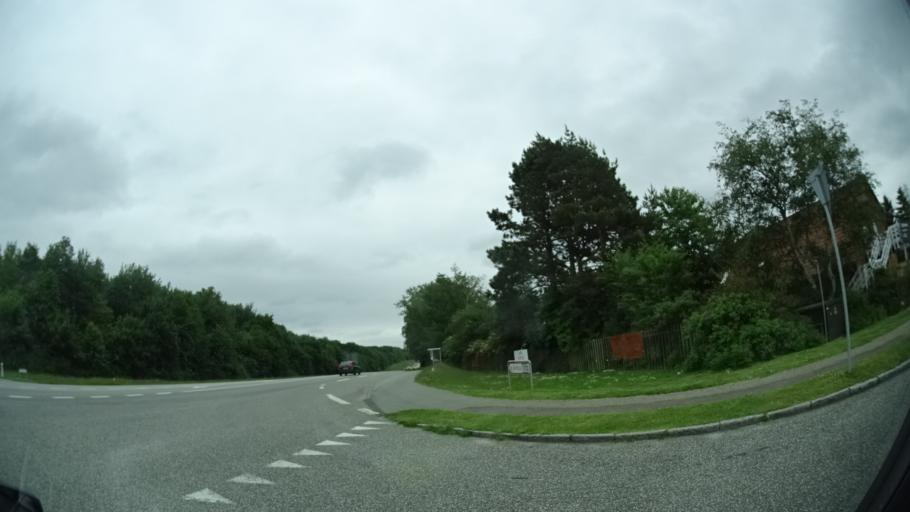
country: DK
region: Central Jutland
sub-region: Arhus Kommune
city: Kolt
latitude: 56.1020
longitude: 10.0703
